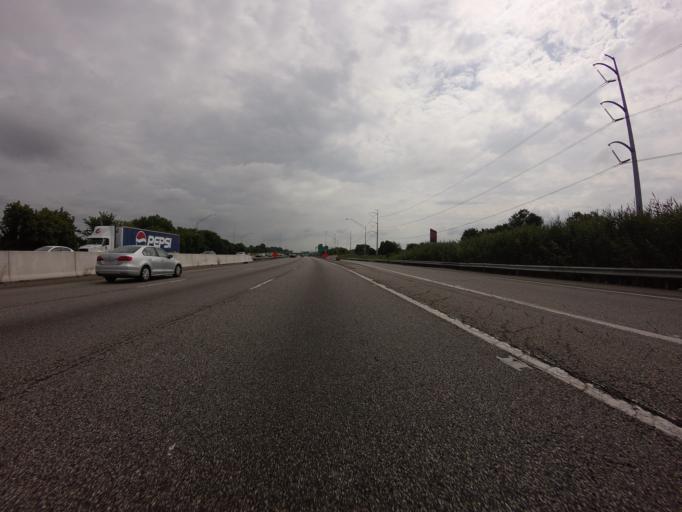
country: US
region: Pennsylvania
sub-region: Delaware County
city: Prospect Park
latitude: 39.8689
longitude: -75.3070
